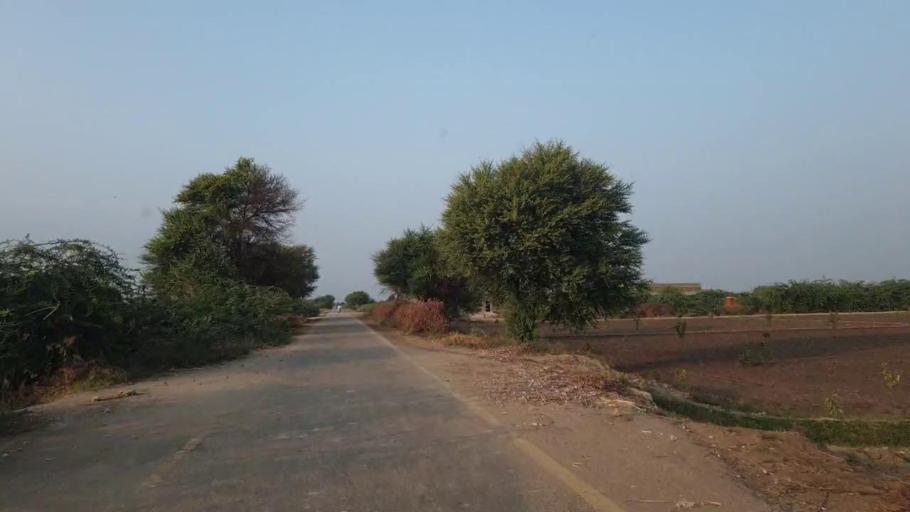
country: PK
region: Sindh
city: Tando Ghulam Ali
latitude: 25.0864
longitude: 68.9586
